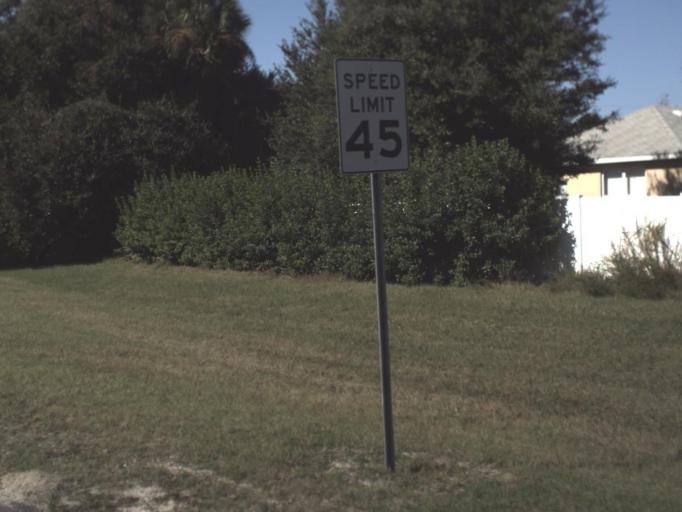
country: US
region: Florida
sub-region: Flagler County
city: Palm Coast
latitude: 29.5986
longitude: -81.2518
